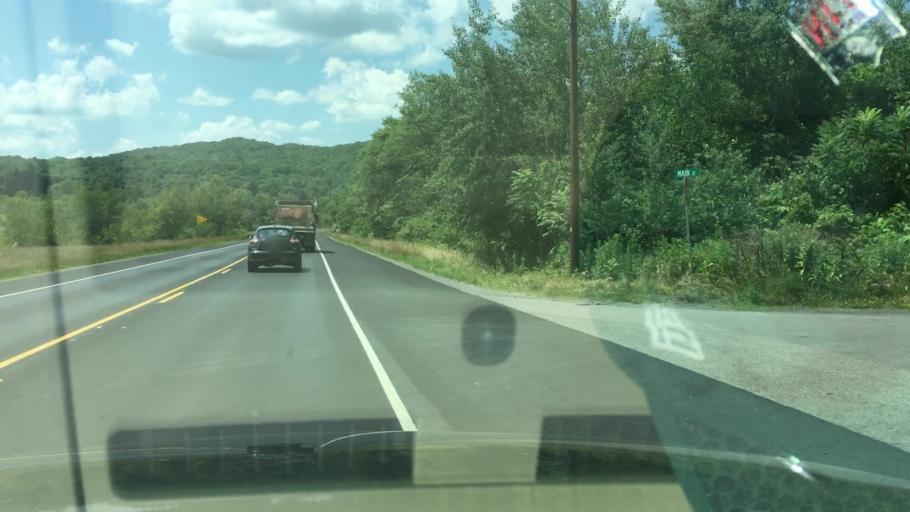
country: US
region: Pennsylvania
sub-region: Northumberland County
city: Mount Carmel
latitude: 40.7682
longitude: -76.4365
